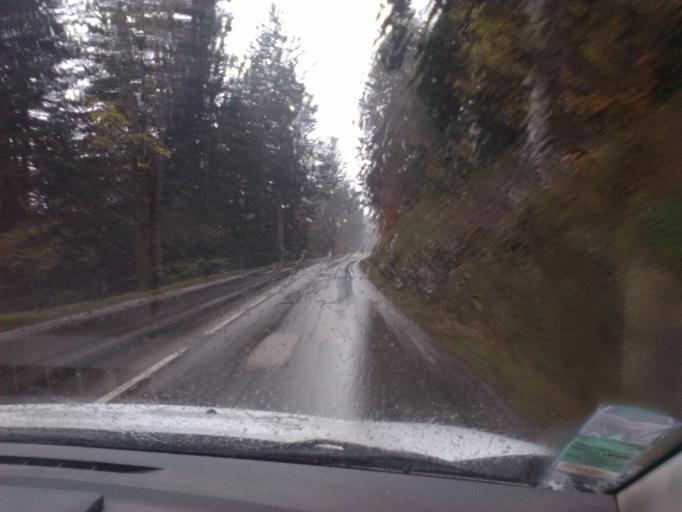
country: FR
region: Lorraine
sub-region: Departement des Vosges
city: Xonrupt-Longemer
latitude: 48.0692
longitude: 6.9622
